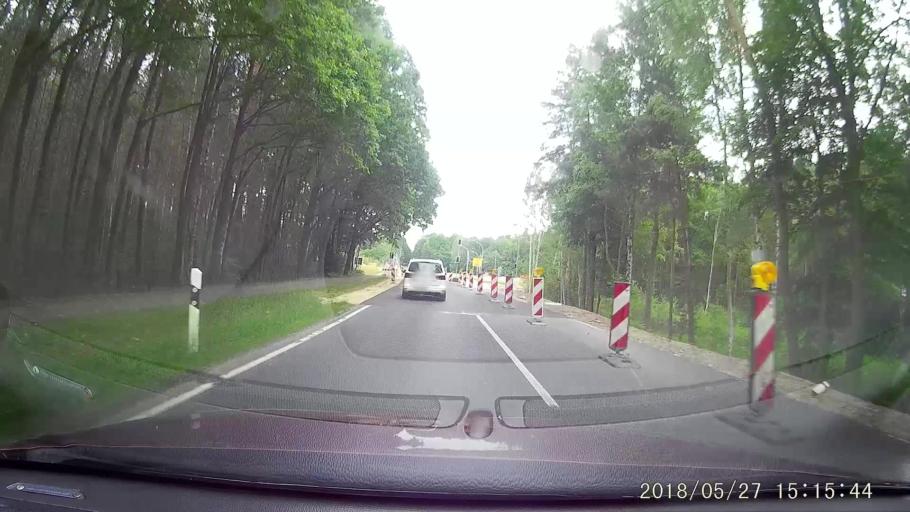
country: DE
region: Saxony
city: Niesky
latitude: 51.2800
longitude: 14.8160
